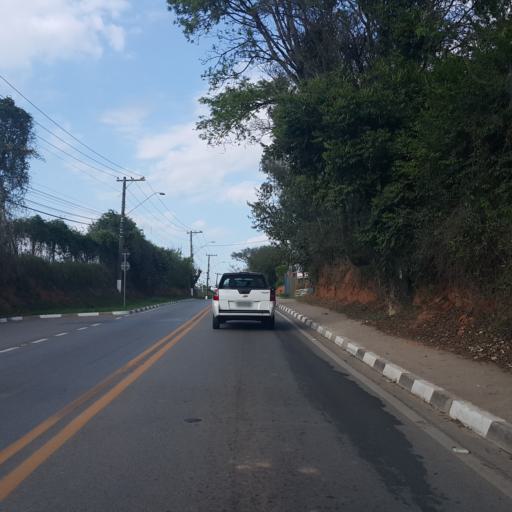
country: BR
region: Sao Paulo
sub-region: Louveira
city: Louveira
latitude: -23.0788
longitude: -46.9672
